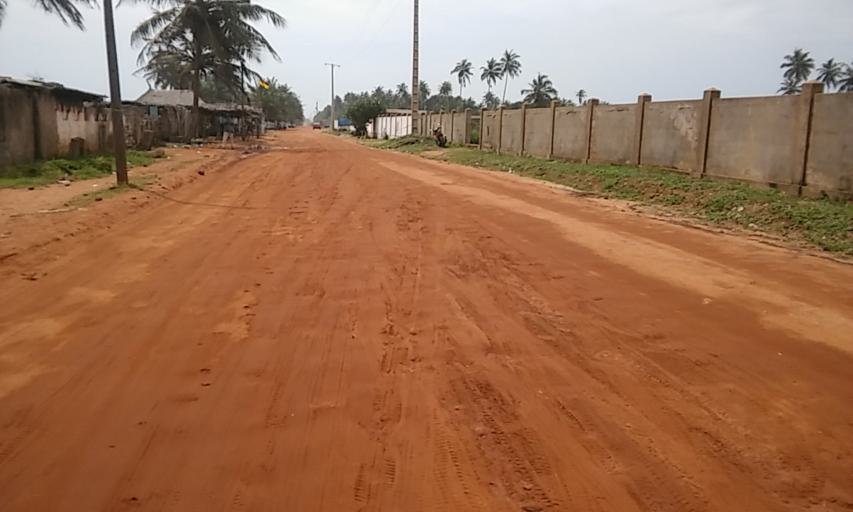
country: CI
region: Sud-Comoe
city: Grand-Bassam
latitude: 5.1973
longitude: -3.7521
